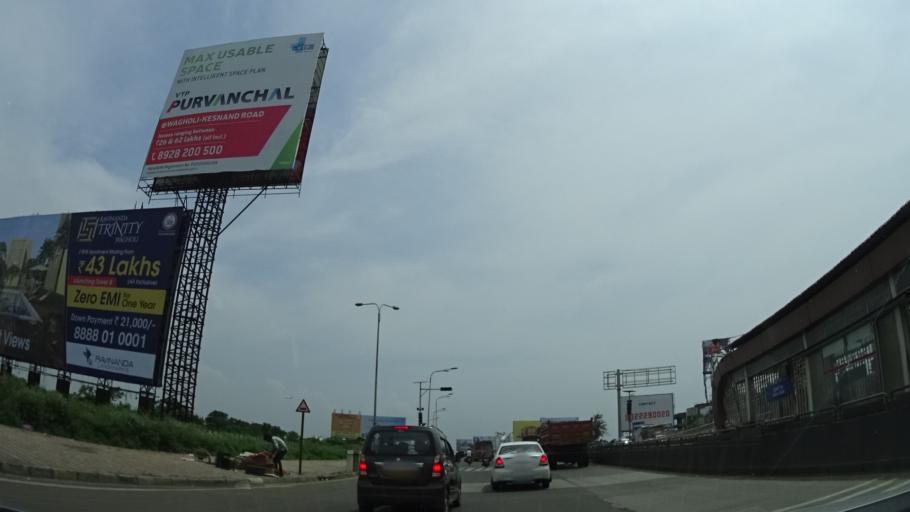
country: IN
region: Maharashtra
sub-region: Pune Division
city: Lohogaon
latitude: 18.5679
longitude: 73.9474
